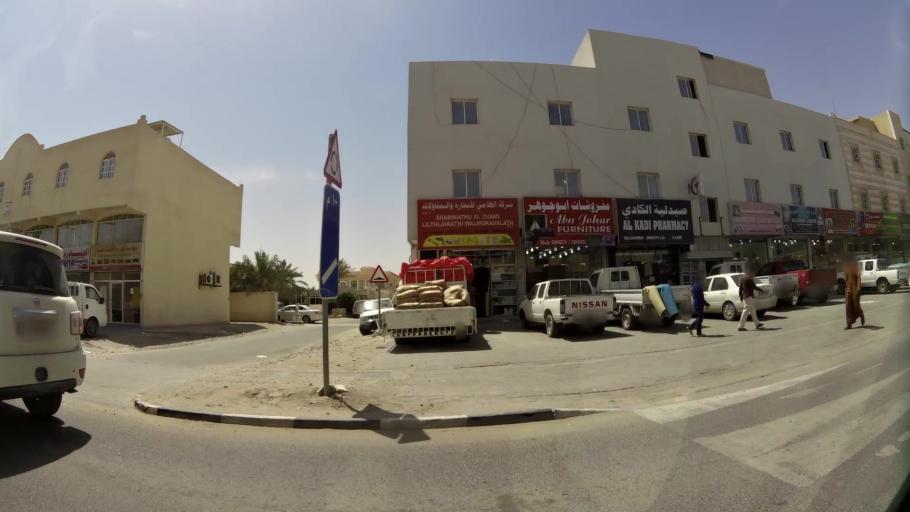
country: QA
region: Baladiyat ar Rayyan
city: Ar Rayyan
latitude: 25.2664
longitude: 51.4098
